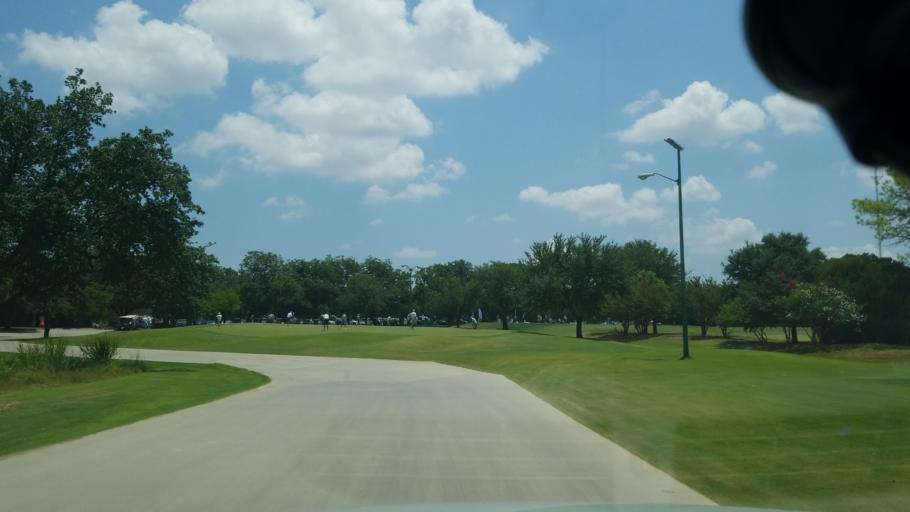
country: US
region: Texas
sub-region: Dallas County
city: Carrollton
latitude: 32.9625
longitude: -96.8719
